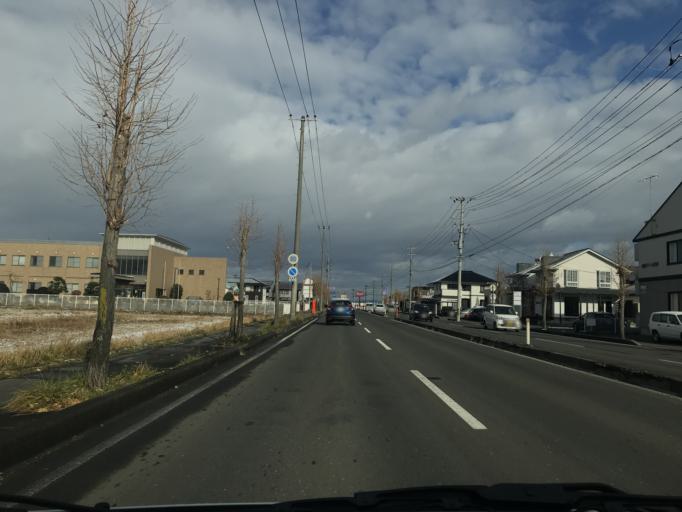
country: JP
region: Iwate
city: Mizusawa
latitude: 39.1329
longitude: 141.1266
